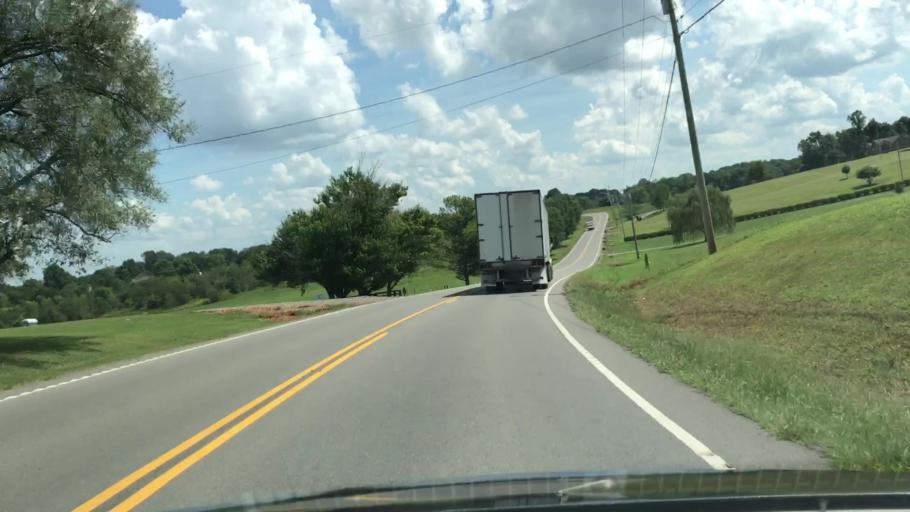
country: US
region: Tennessee
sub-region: Robertson County
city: Cross Plains
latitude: 36.5406
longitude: -86.6687
